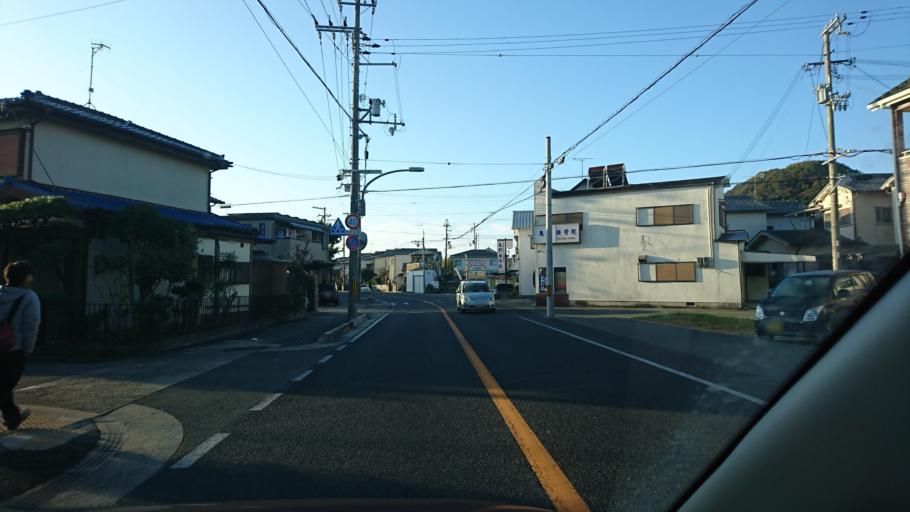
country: JP
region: Hyogo
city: Shirahamacho-usazakiminami
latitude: 34.7856
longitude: 134.7709
